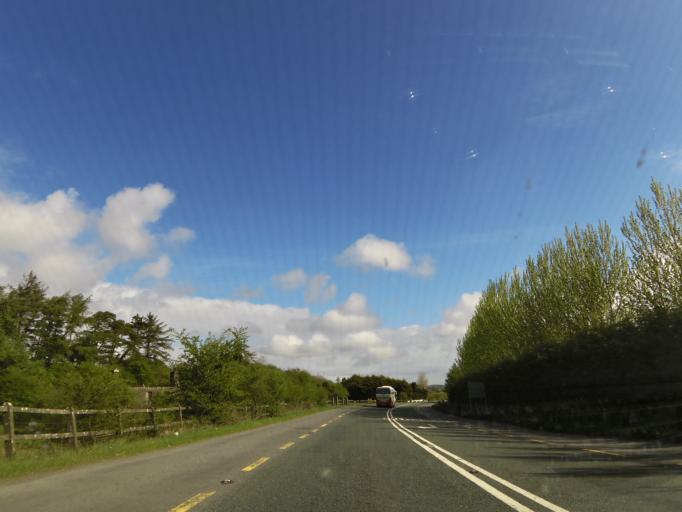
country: IE
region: Connaught
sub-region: Maigh Eo
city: Swinford
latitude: 53.8631
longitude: -8.8549
